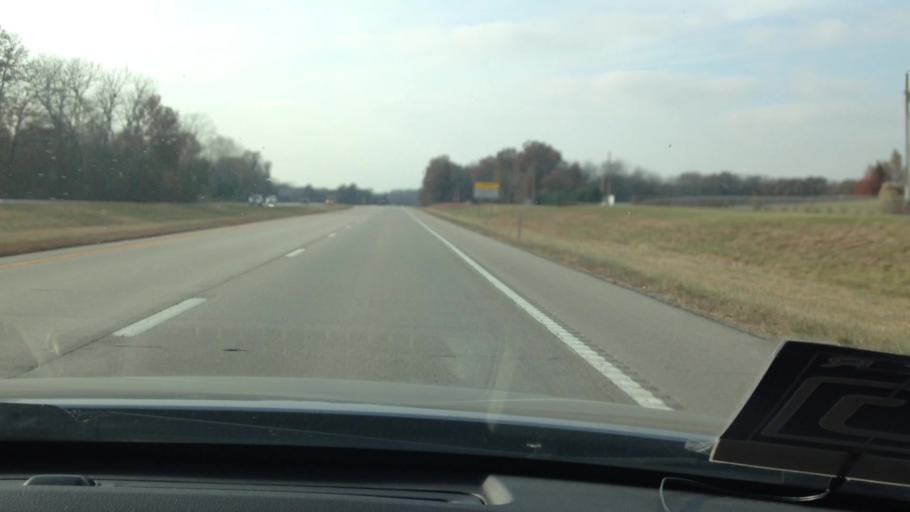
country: US
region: Missouri
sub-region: Cass County
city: Garden City
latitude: 38.5053
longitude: -94.0868
